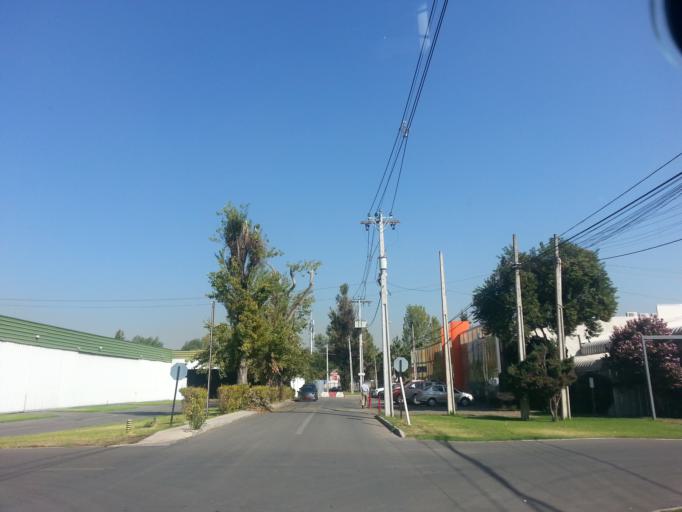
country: CL
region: Santiago Metropolitan
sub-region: Provincia de Santiago
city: Villa Presidente Frei, Nunoa, Santiago, Chile
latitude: -33.4614
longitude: -70.5506
